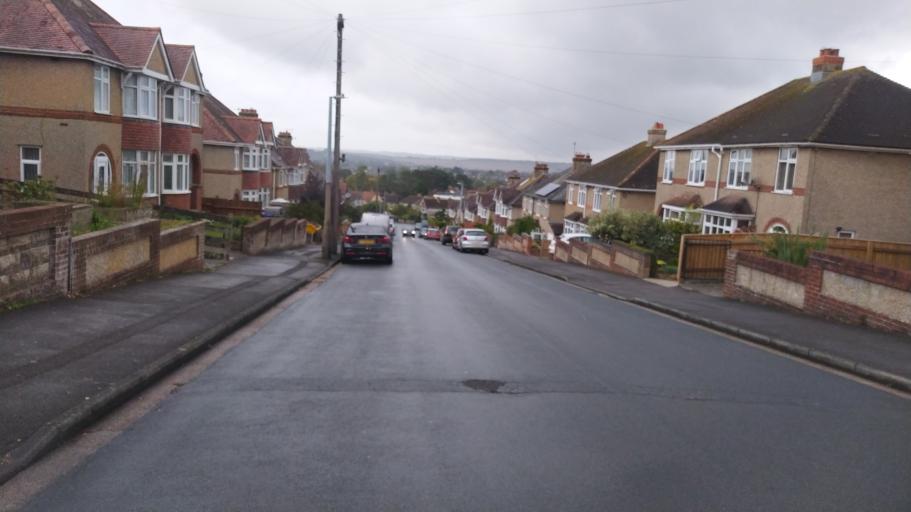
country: GB
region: England
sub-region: Wiltshire
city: Salisbury
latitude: 51.0859
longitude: -1.7949
